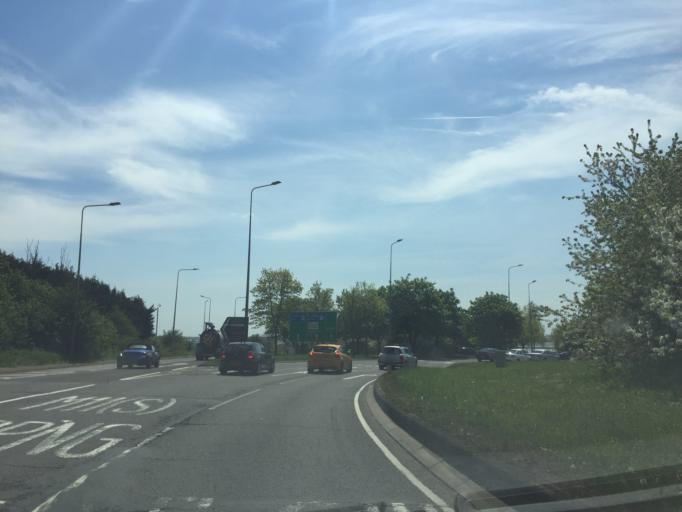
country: GB
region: England
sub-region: Essex
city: Harlow
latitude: 51.7433
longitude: 0.1394
